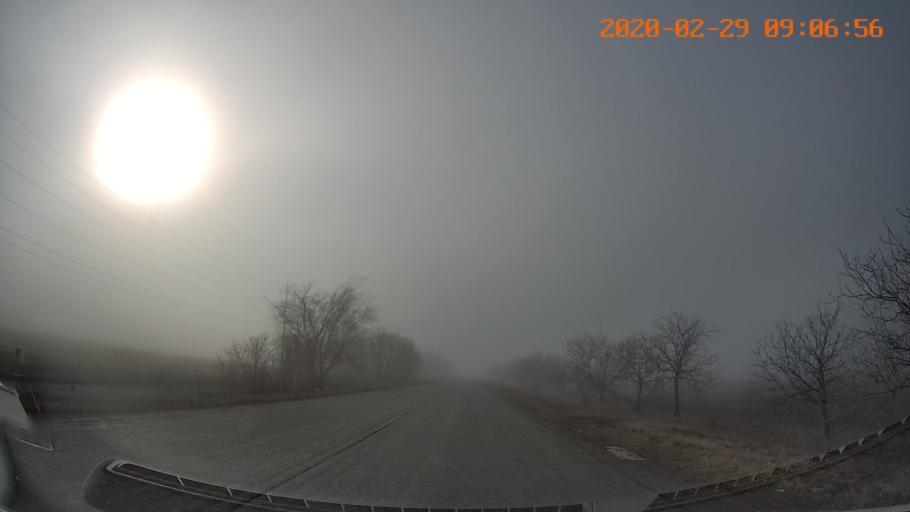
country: MD
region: Telenesti
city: Tiraspolul Nou
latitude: 46.8691
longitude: 29.7467
